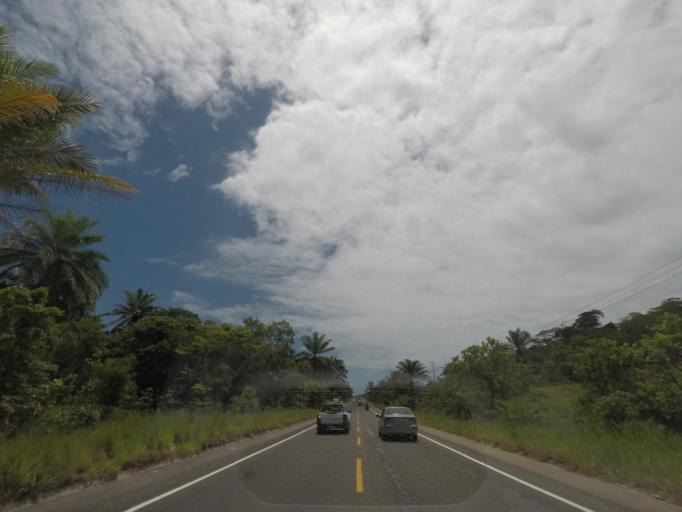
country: BR
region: Bahia
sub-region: Itaparica
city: Itaparica
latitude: -12.9701
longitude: -38.6357
